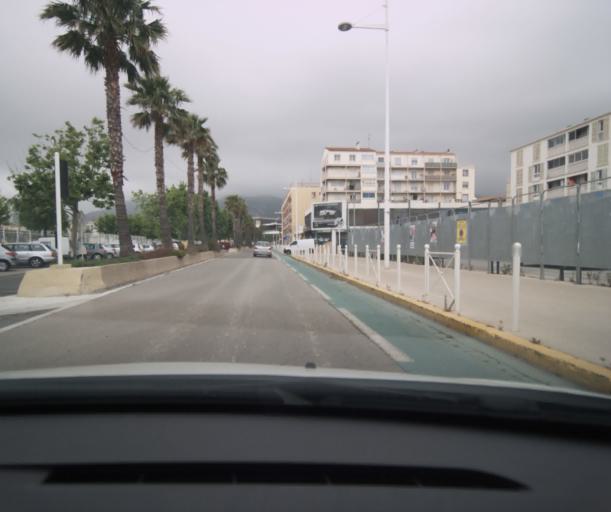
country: FR
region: Provence-Alpes-Cote d'Azur
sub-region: Departement du Var
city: Toulon
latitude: 43.1158
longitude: 5.9354
